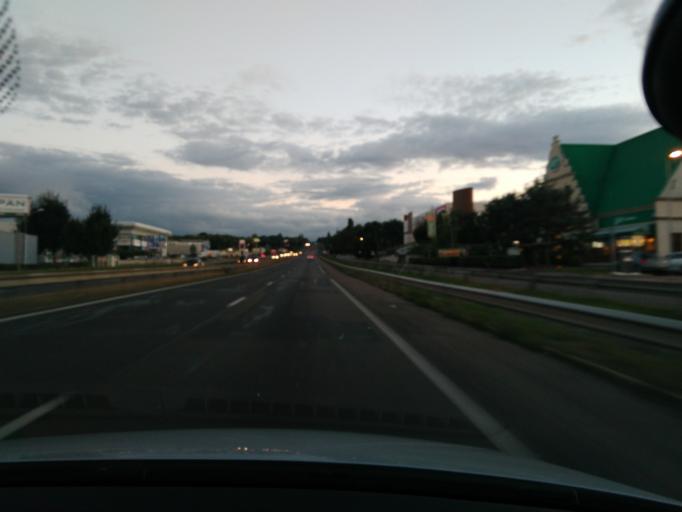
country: FR
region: Ile-de-France
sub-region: Departement de Seine-et-Marne
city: Nanteuil-les-Meaux
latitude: 48.9394
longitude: 2.8796
